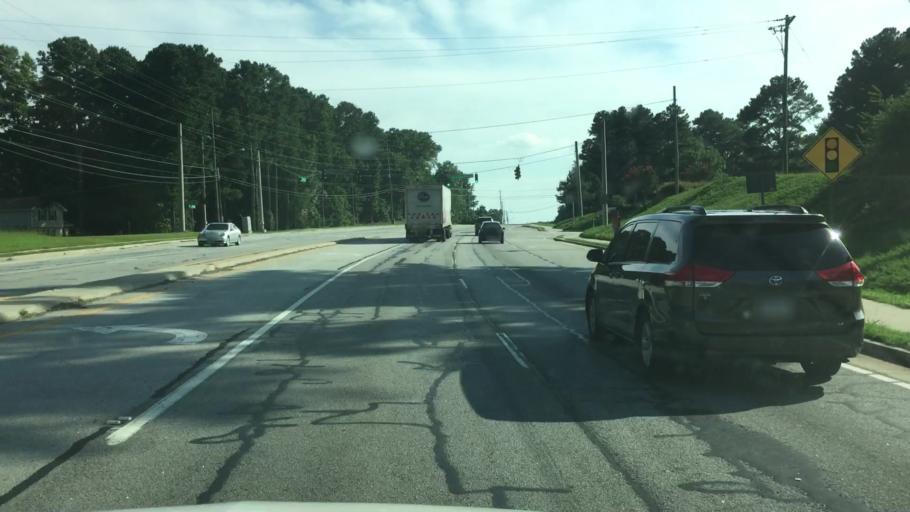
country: US
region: Georgia
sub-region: Gwinnett County
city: Snellville
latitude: 33.8218
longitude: -84.0336
